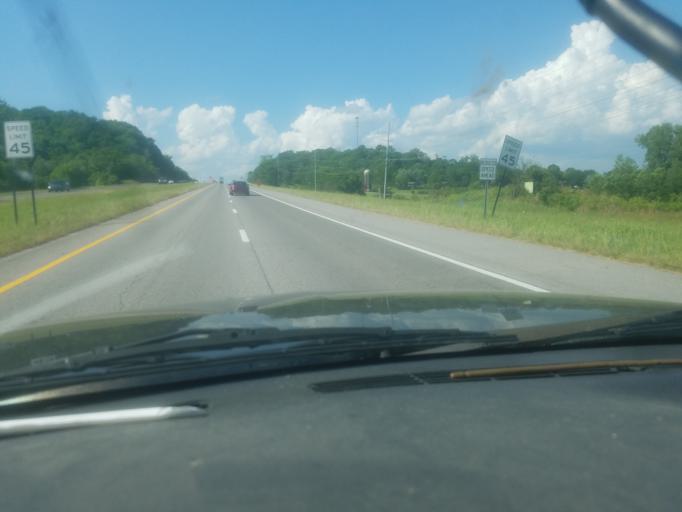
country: US
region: Tennessee
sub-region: Maury County
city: Mount Pleasant
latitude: 35.5307
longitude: -87.2219
